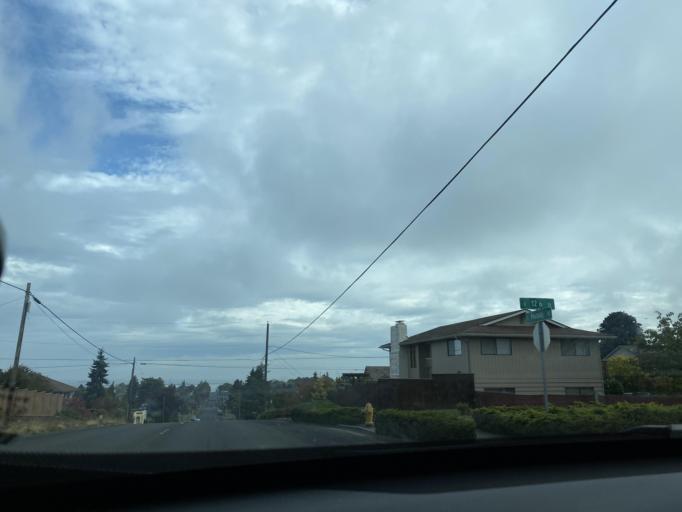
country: US
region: Washington
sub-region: Clallam County
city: Port Angeles
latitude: 48.1071
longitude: -123.4368
